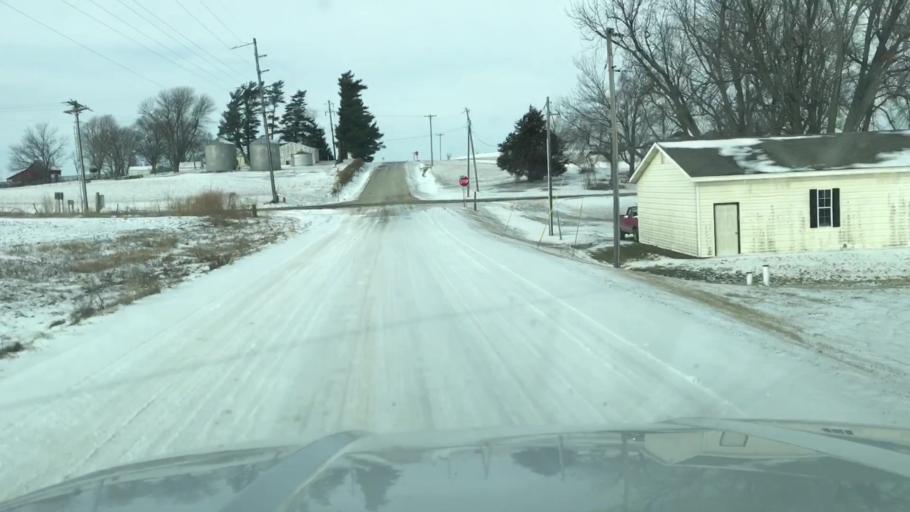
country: US
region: Missouri
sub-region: Holt County
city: Mound City
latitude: 40.1301
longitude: -95.0882
